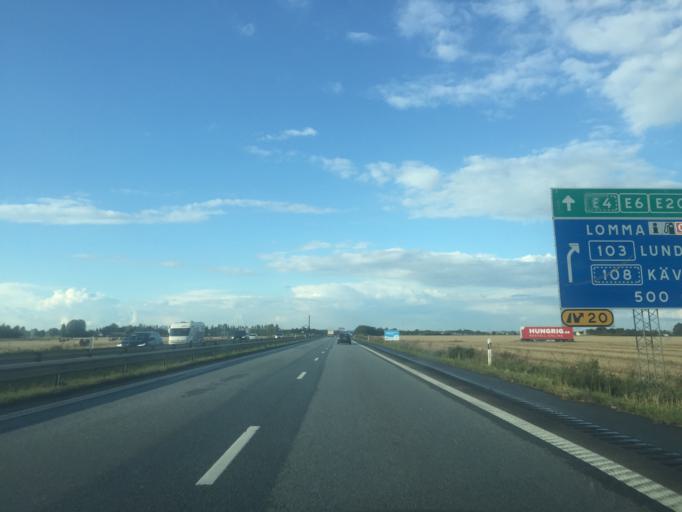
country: SE
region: Skane
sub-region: Lomma Kommun
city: Lomma
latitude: 55.6777
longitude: 13.0988
